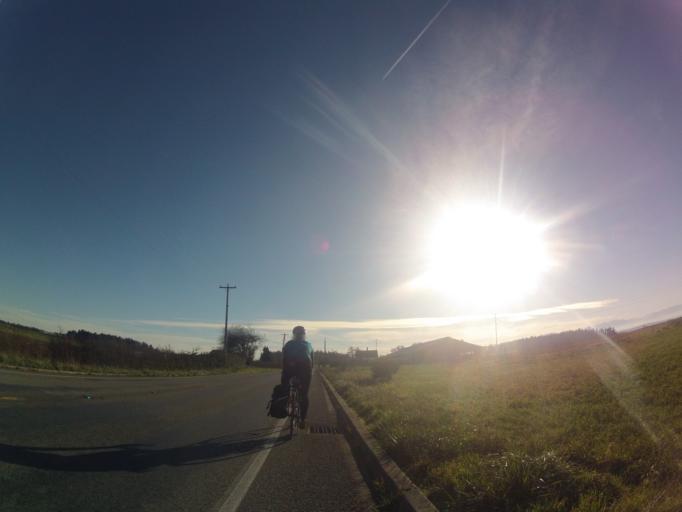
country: US
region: Washington
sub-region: Island County
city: Coupeville
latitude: 48.2007
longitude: -122.6862
